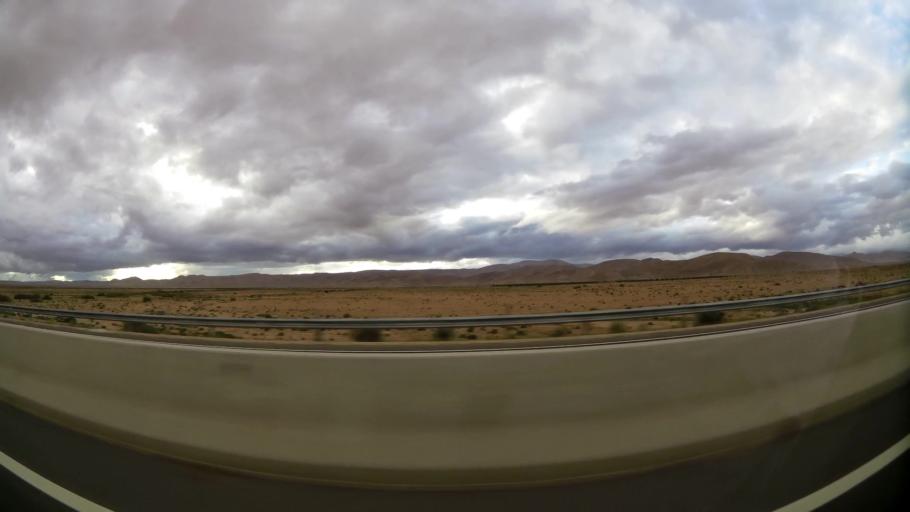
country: MA
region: Taza-Al Hoceima-Taounate
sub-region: Taza
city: Guercif
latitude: 34.3223
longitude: -3.5742
